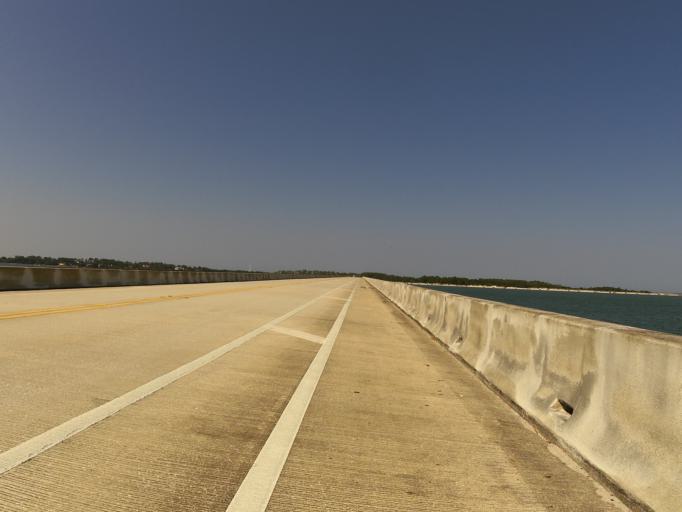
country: US
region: Florida
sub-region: Nassau County
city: Fernandina Beach
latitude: 30.5143
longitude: -81.4547
